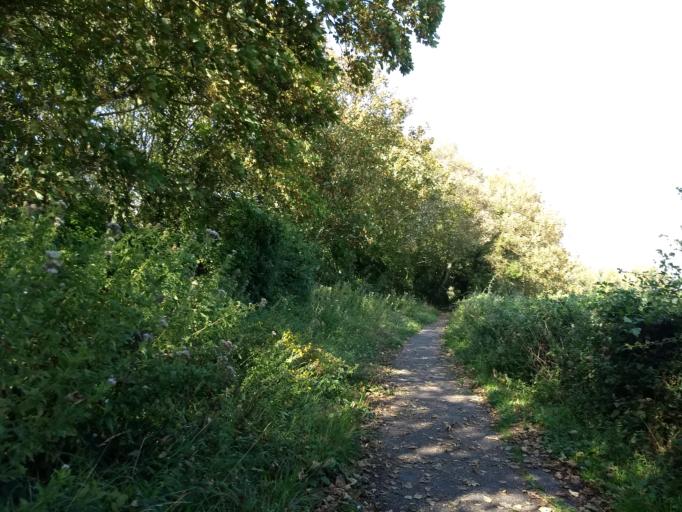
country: GB
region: England
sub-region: Isle of Wight
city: Totland
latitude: 50.7008
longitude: -1.5302
